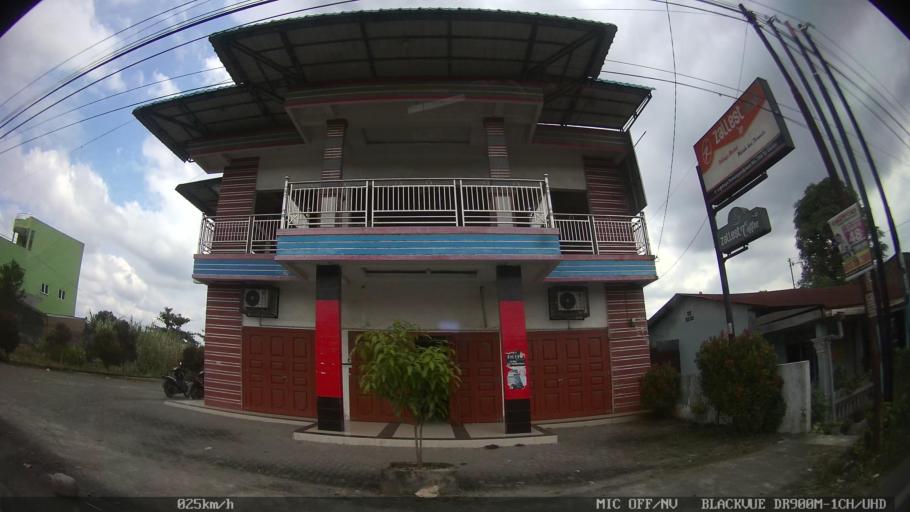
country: ID
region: North Sumatra
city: Sunggal
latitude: 3.6183
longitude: 98.6167
